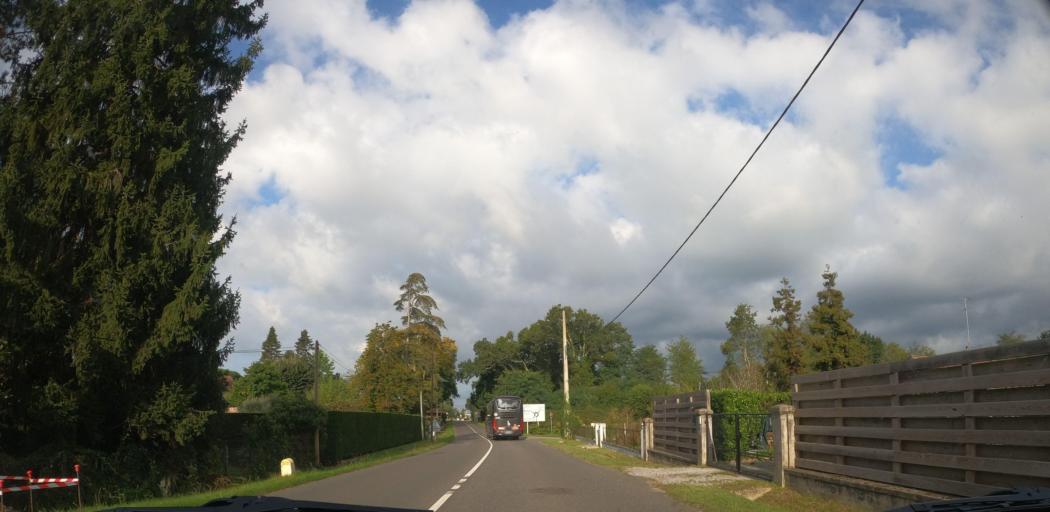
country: FR
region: Aquitaine
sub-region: Departement des Landes
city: Soustons
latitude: 43.7472
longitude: -1.3164
